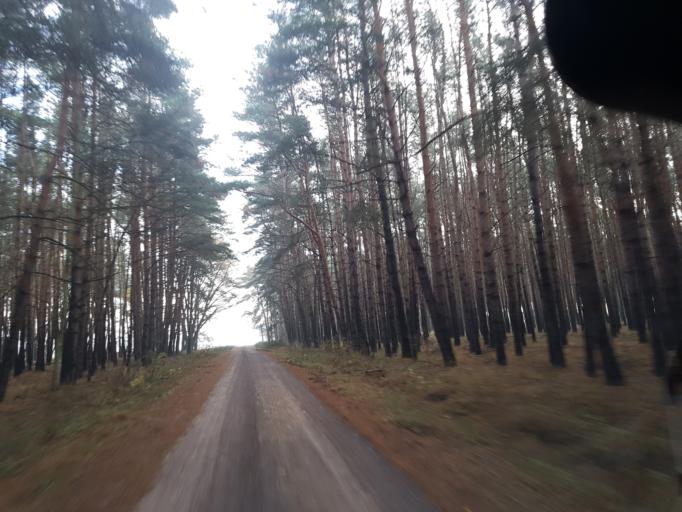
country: DE
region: Saxony-Anhalt
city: Seyda
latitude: 51.8904
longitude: 12.8768
